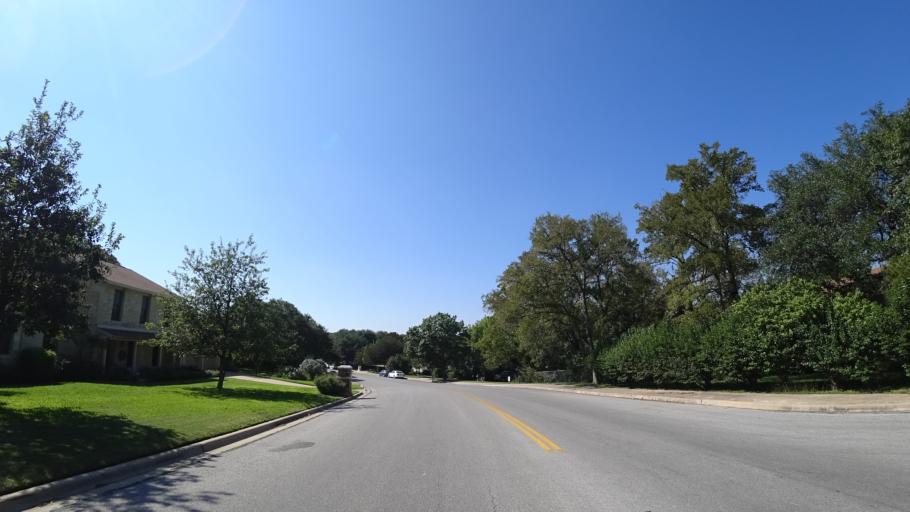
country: US
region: Texas
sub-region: Travis County
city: Rollingwood
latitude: 30.2535
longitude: -97.7894
